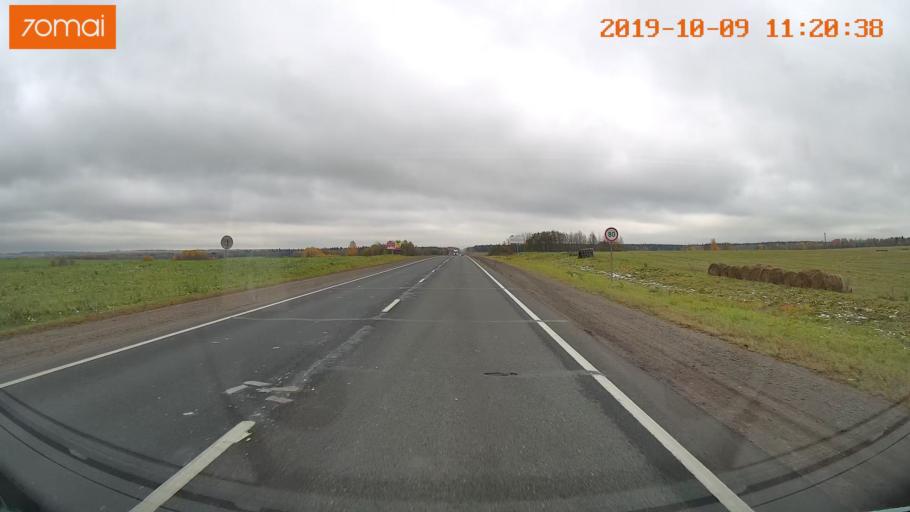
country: RU
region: Vologda
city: Vologda
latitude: 59.1475
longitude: 39.9408
